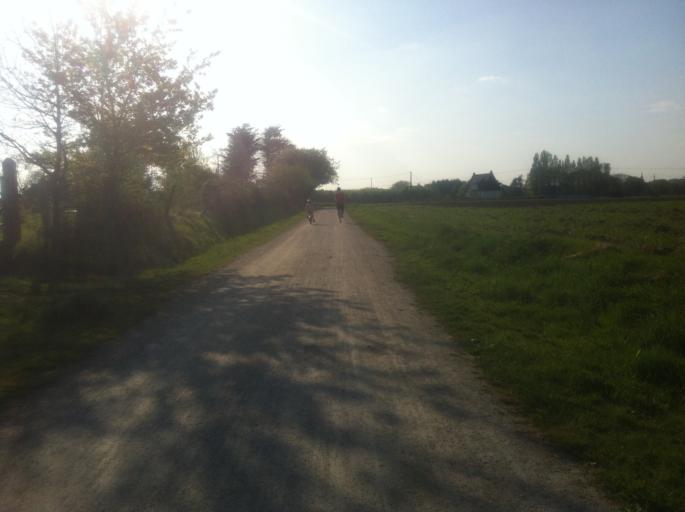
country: FR
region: Brittany
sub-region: Departement d'Ille-et-Vilaine
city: Bruz
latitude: 48.0123
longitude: -1.7230
